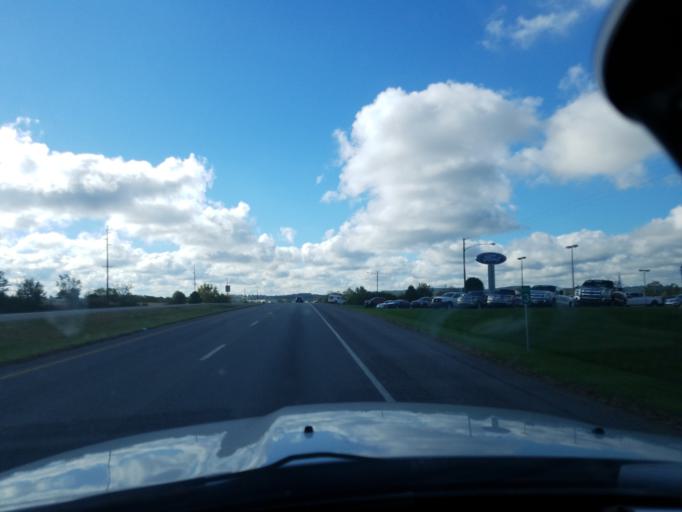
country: US
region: Kentucky
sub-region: Boyle County
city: Danville
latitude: 37.6458
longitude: -84.8031
